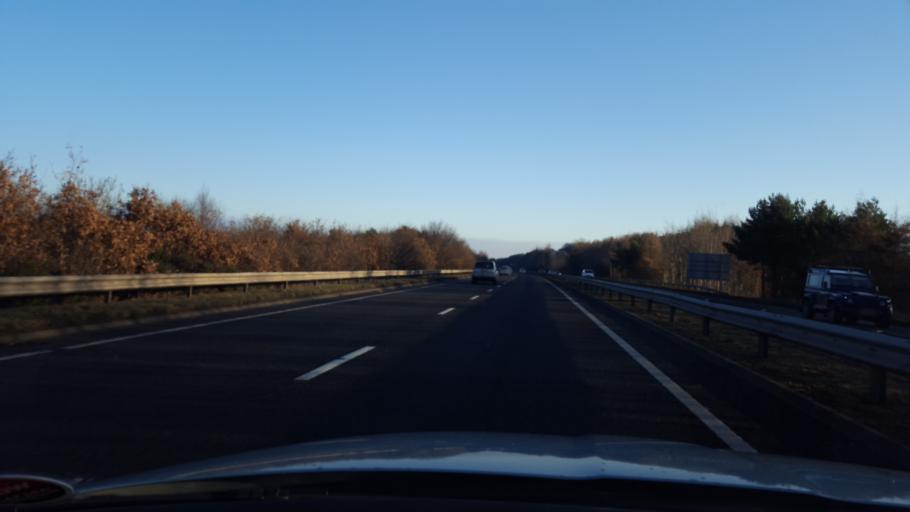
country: GB
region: Scotland
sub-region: Fife
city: Cardenden
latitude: 56.1259
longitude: -3.2702
